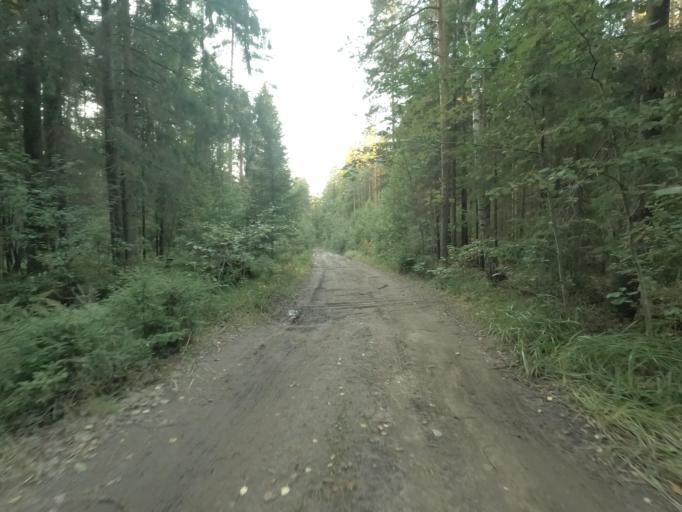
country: RU
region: Leningrad
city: Otradnoye
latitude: 59.8255
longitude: 30.8197
